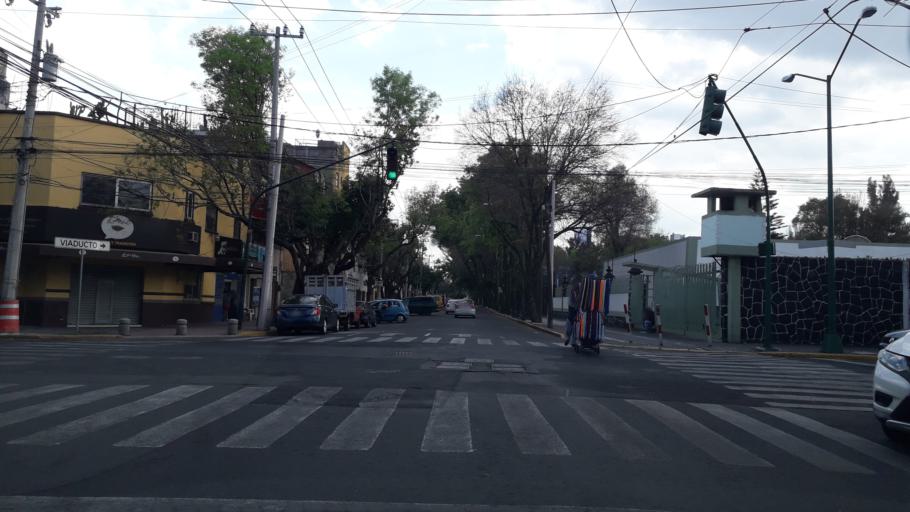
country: MX
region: Mexico City
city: Mexico City
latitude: 19.4059
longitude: -99.1339
